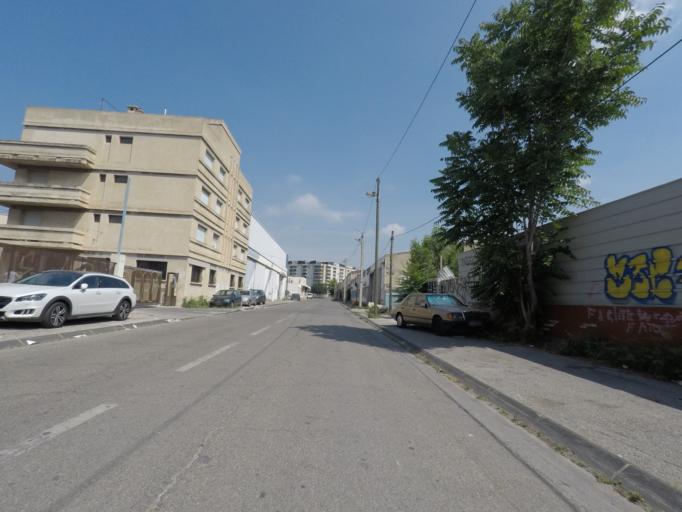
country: FR
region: Provence-Alpes-Cote d'Azur
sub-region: Departement des Bouches-du-Rhone
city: Marseille 10
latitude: 43.2753
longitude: 5.4073
